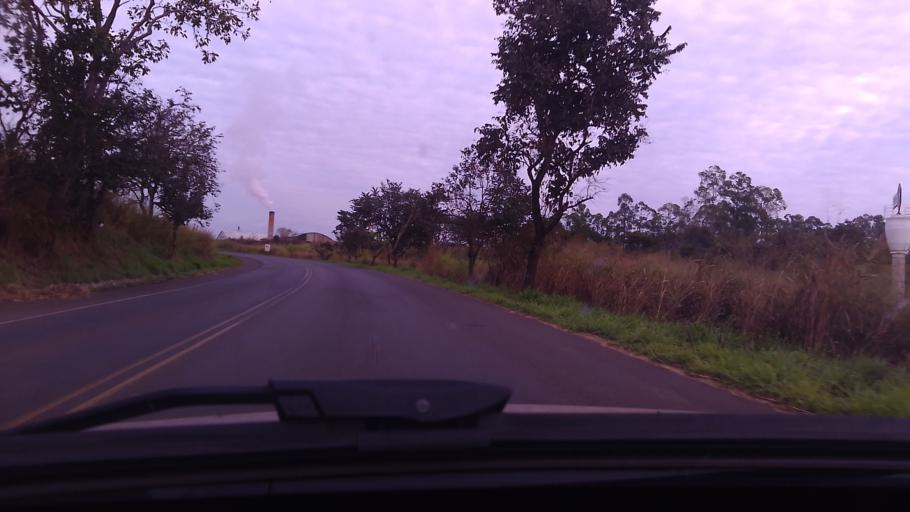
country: BR
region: Goias
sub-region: Mineiros
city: Mineiros
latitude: -17.5785
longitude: -52.5084
